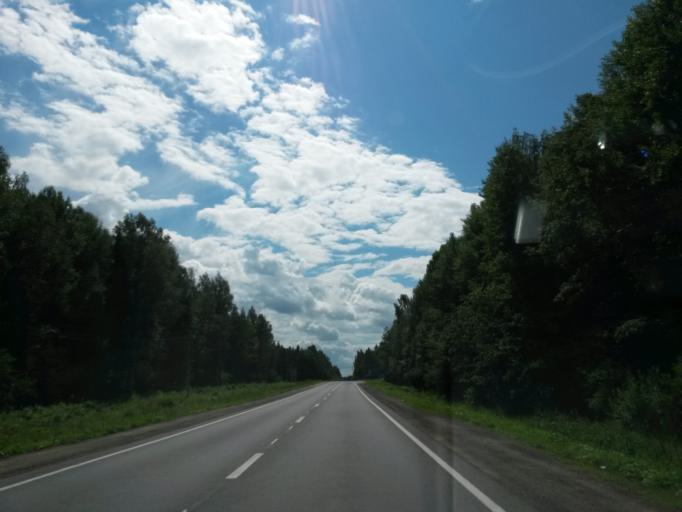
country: RU
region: Jaroslavl
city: Gavrilov-Yam
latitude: 57.2749
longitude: 39.9505
